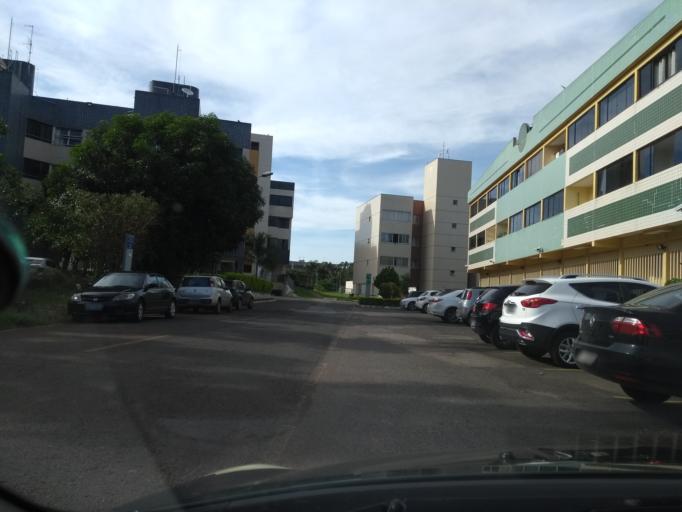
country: BR
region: Federal District
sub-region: Brasilia
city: Brasilia
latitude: -15.7922
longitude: -47.9307
